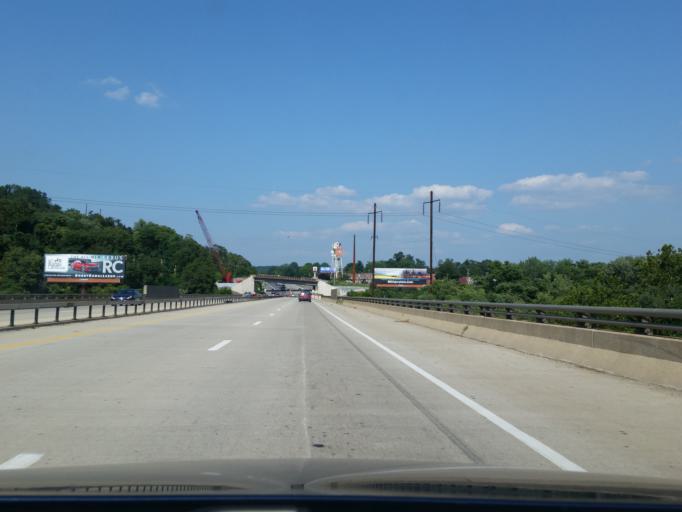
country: US
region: Pennsylvania
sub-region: Lancaster County
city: Columbia
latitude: 40.0370
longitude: -76.5159
